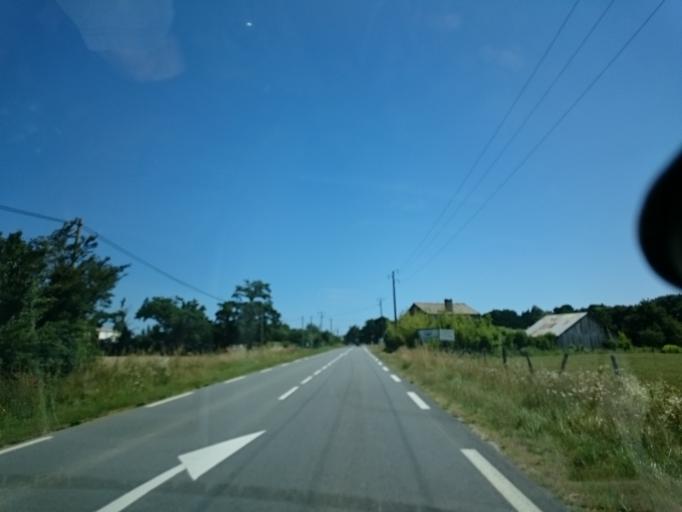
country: FR
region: Brittany
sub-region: Departement d'Ille-et-Vilaine
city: Saint-Pere
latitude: 48.5829
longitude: -1.9119
